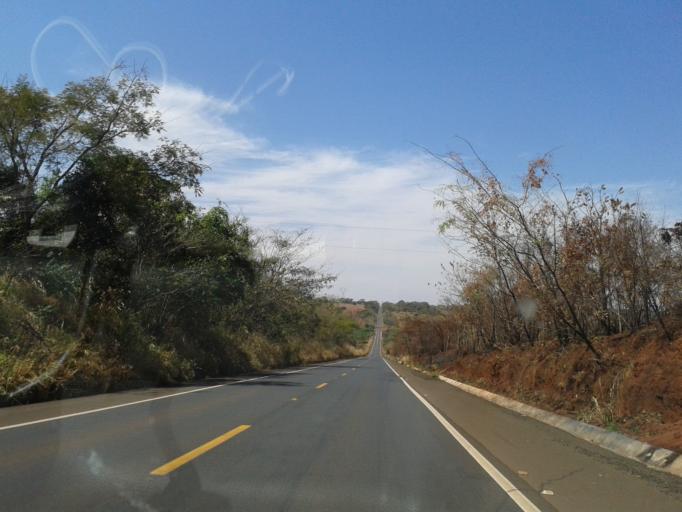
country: BR
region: Minas Gerais
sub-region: Santa Vitoria
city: Santa Vitoria
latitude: -18.8892
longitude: -50.0102
